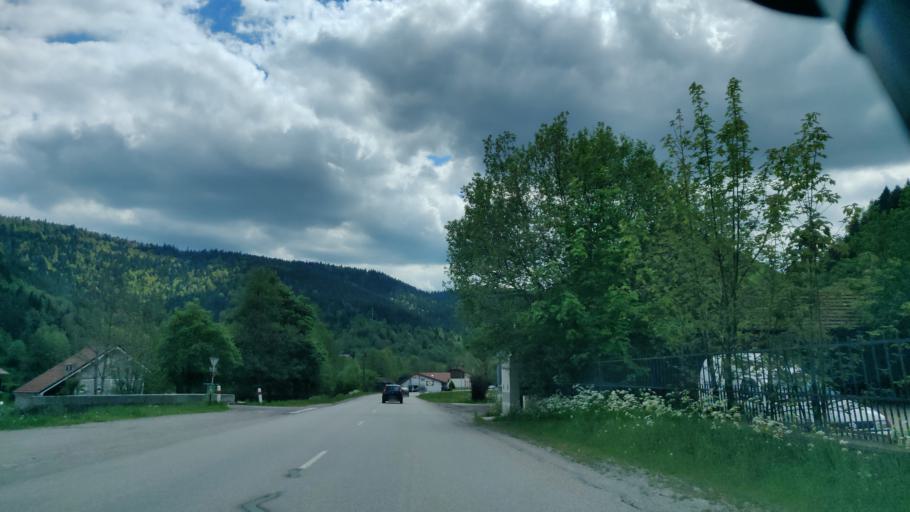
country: FR
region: Lorraine
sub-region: Departement des Vosges
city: La Bresse
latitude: 48.0080
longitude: 6.9374
